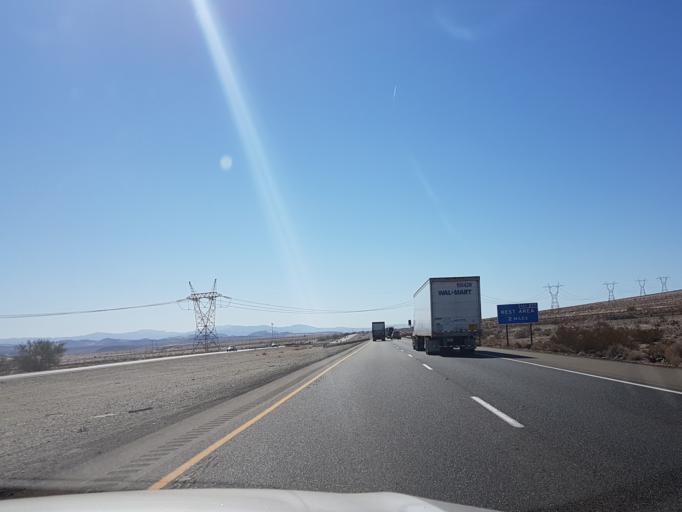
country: US
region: California
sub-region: San Bernardino County
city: Fort Irwin
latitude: 35.0532
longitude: -116.4398
